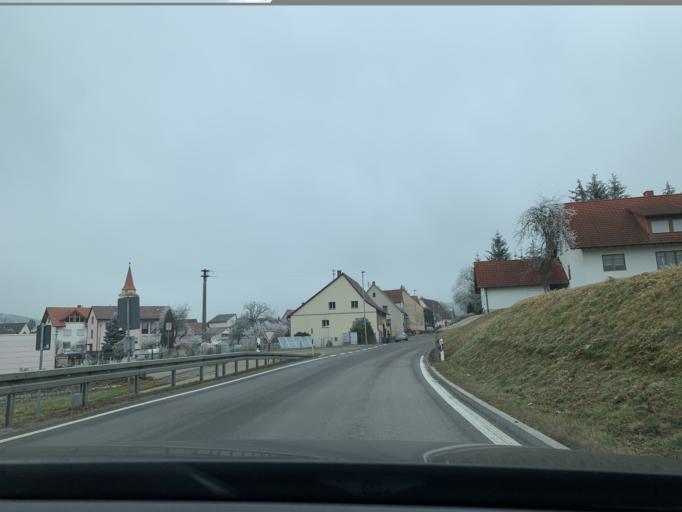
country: DE
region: Baden-Wuerttemberg
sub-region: Freiburg Region
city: Geisingen
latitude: 47.8847
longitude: 8.6563
